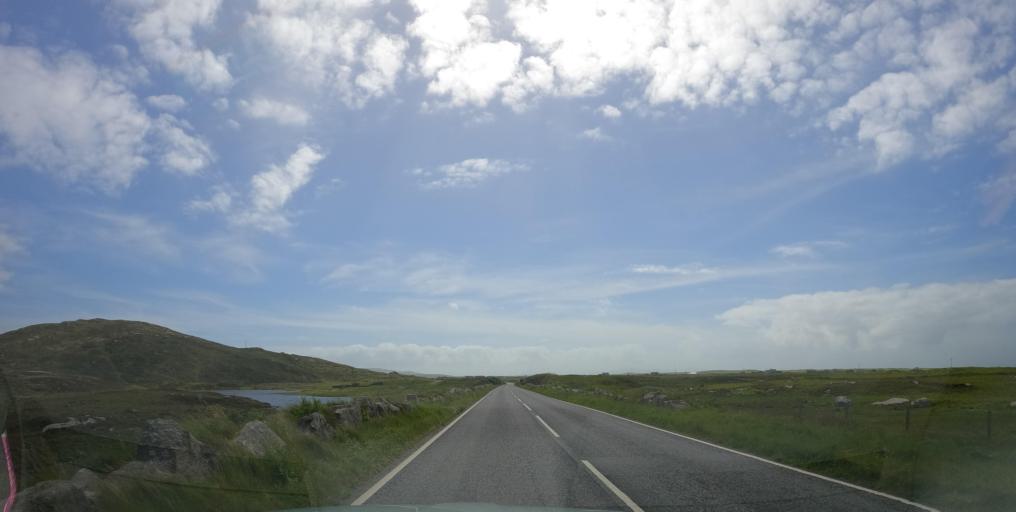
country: GB
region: Scotland
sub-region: Eilean Siar
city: Isle of South Uist
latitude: 57.1942
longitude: -7.3892
